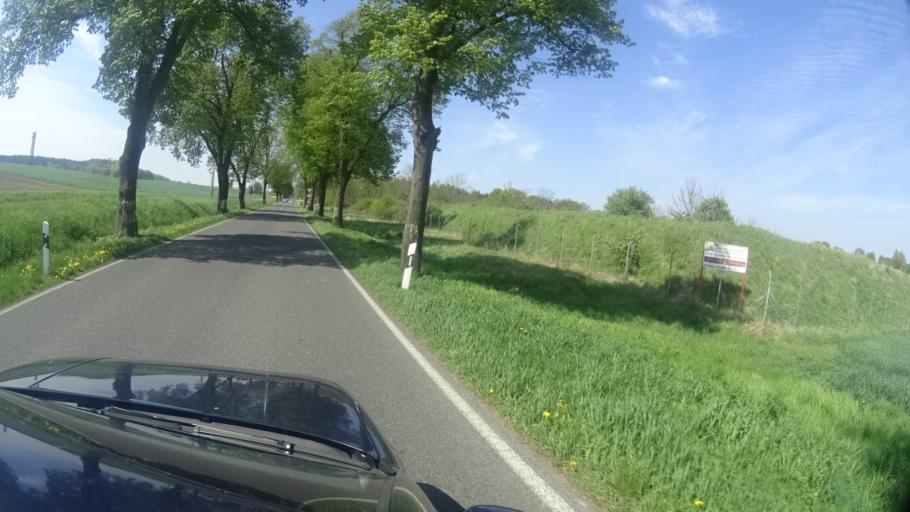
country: DE
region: Brandenburg
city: Rhinow
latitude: 52.7546
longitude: 12.3642
